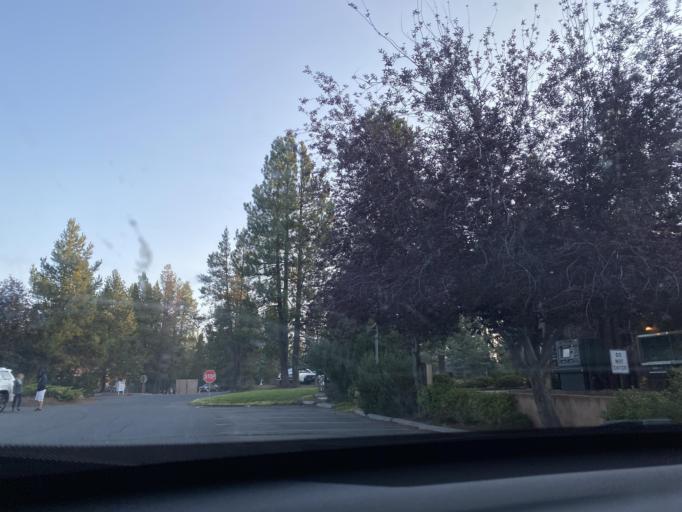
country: US
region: Oregon
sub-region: Deschutes County
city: Sunriver
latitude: 43.8740
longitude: -121.4354
